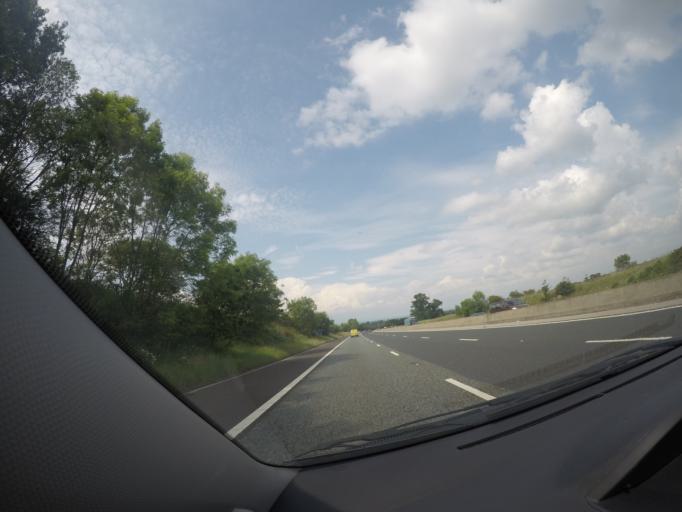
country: GB
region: England
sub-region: Cumbria
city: Scotby
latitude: 54.8334
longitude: -2.8891
